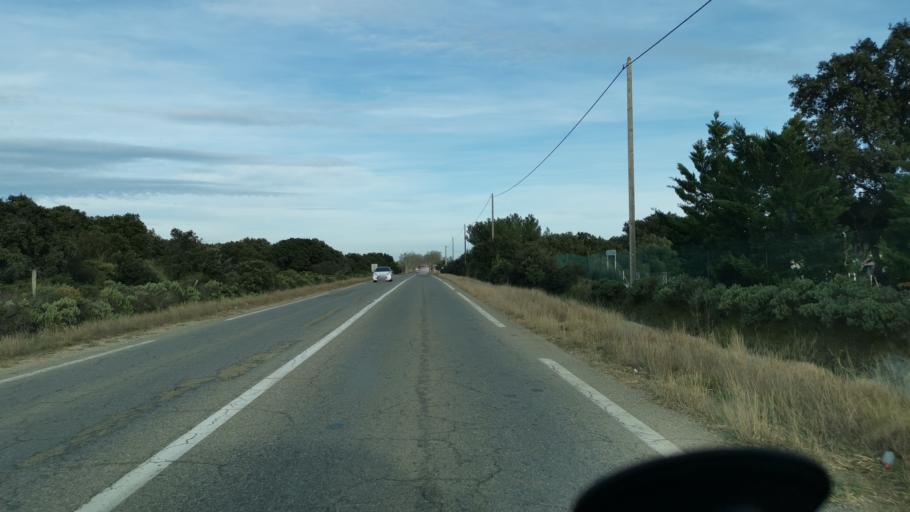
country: FR
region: Provence-Alpes-Cote d'Azur
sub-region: Departement des Bouches-du-Rhone
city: Saint-Martin-de-Crau
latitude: 43.6352
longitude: 4.7803
